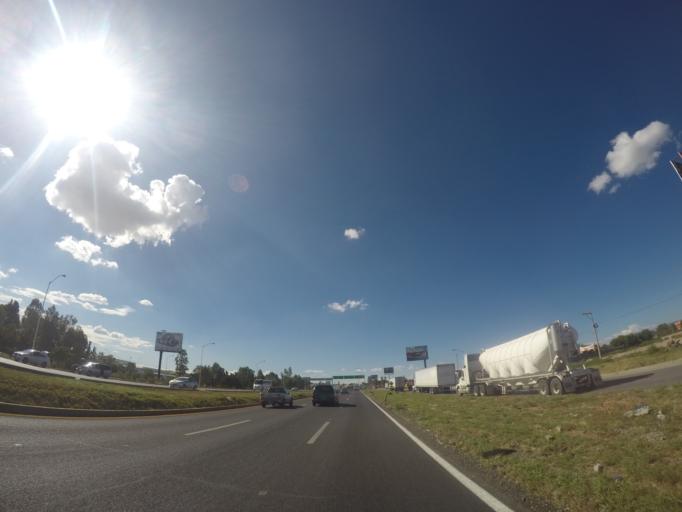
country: MX
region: San Luis Potosi
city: La Pila
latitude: 22.0788
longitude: -100.8755
